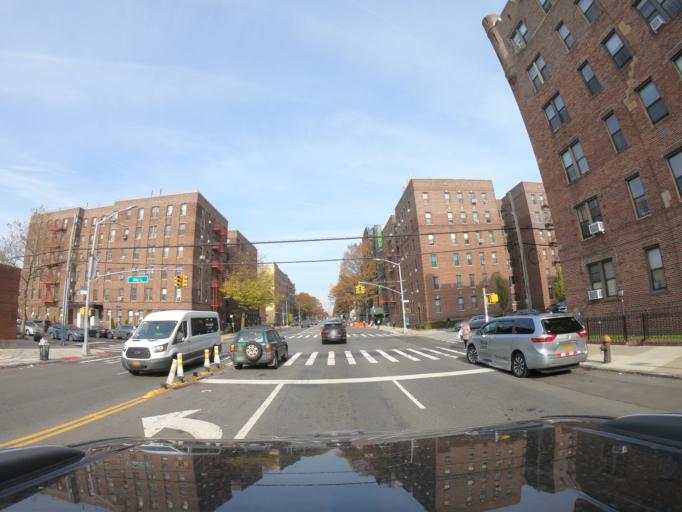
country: US
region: New York
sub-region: Kings County
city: Brooklyn
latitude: 40.6208
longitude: -73.9554
